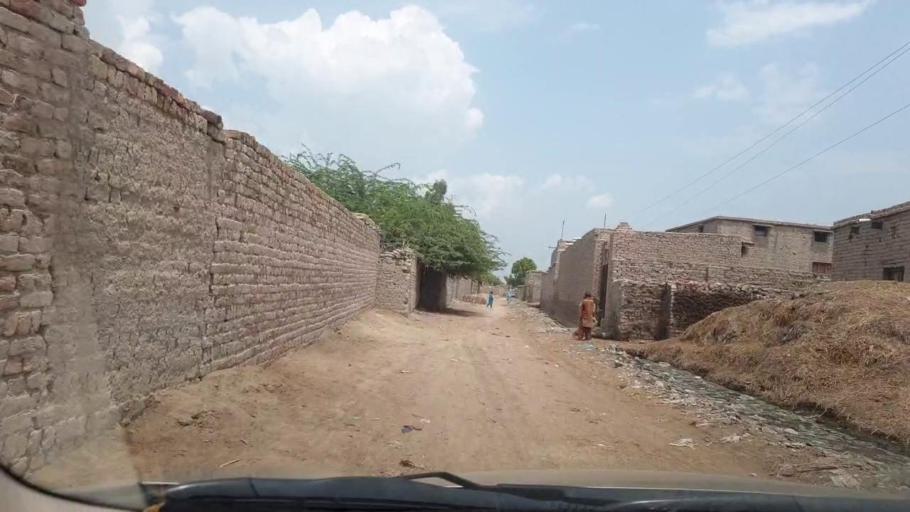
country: PK
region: Sindh
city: Larkana
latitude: 27.5647
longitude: 68.1255
